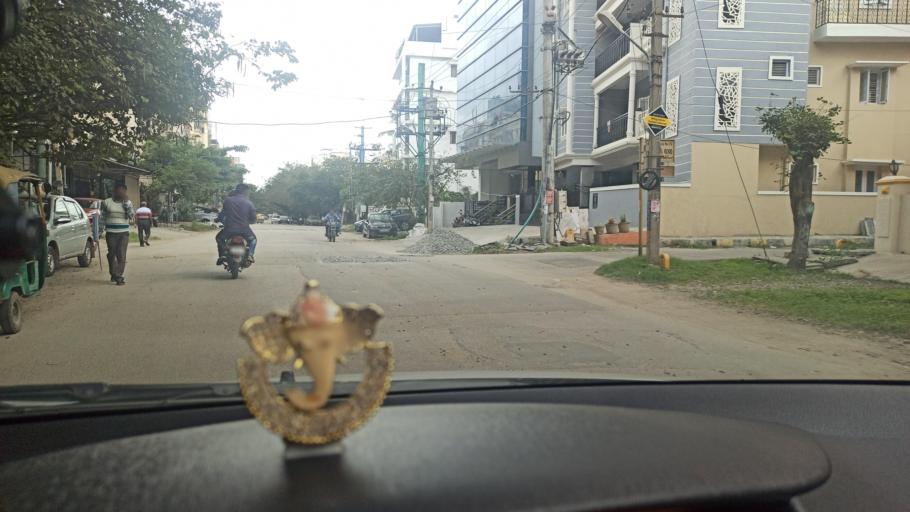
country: IN
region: Karnataka
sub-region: Bangalore Urban
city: Bangalore
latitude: 12.9141
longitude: 77.6276
